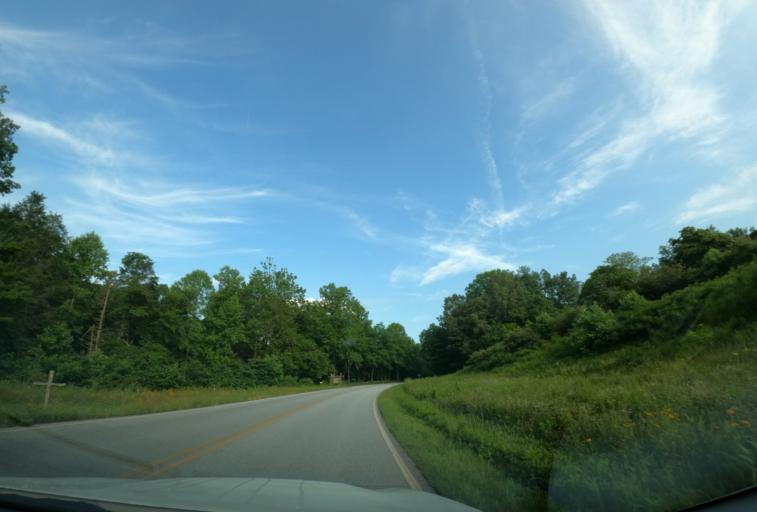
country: US
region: North Carolina
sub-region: Transylvania County
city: Brevard
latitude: 35.2258
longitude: -82.8691
